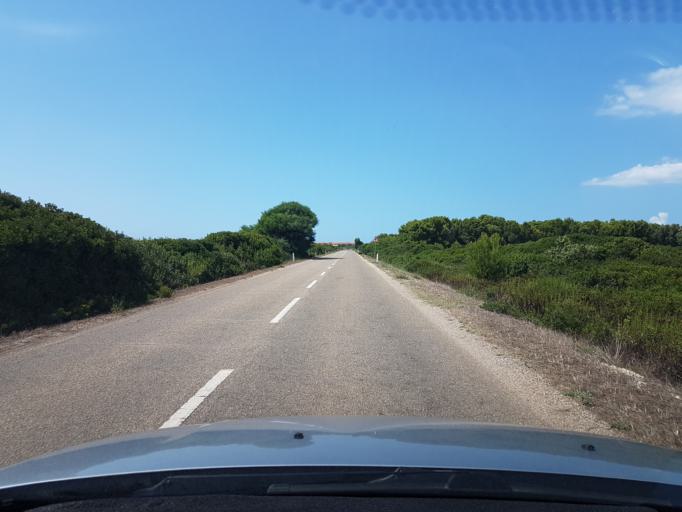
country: IT
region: Sardinia
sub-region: Provincia di Oristano
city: Riola Sardo
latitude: 40.0347
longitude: 8.4227
